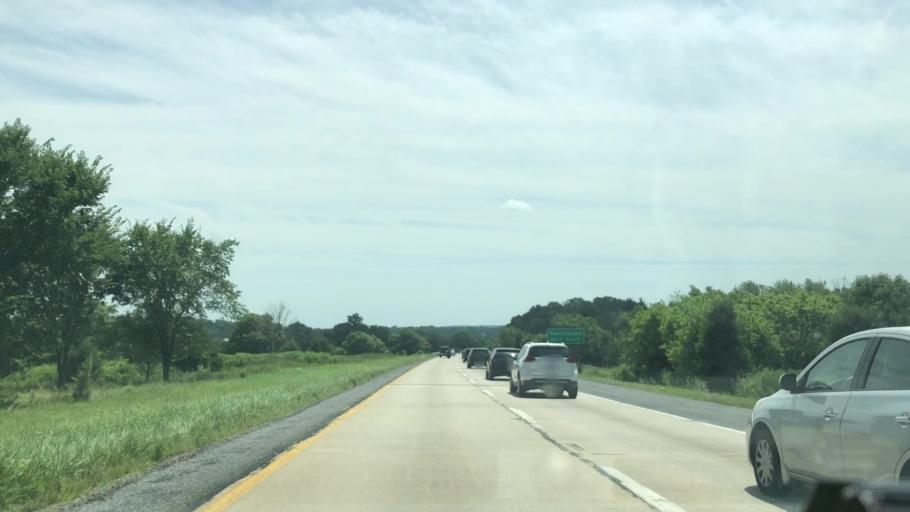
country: US
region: Pennsylvania
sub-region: Montgomery County
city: Audubon
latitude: 40.1441
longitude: -75.4562
